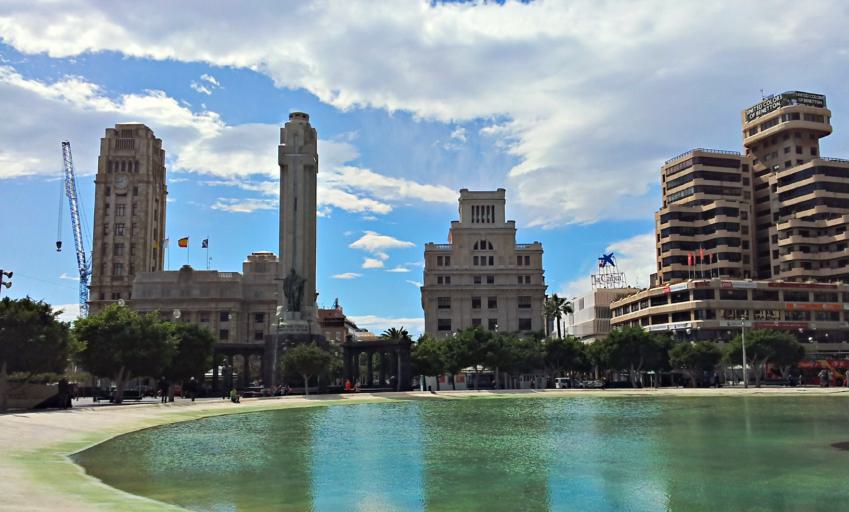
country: ES
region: Canary Islands
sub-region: Provincia de Santa Cruz de Tenerife
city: Santa Cruz de Tenerife
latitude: 28.4675
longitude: -16.2476
